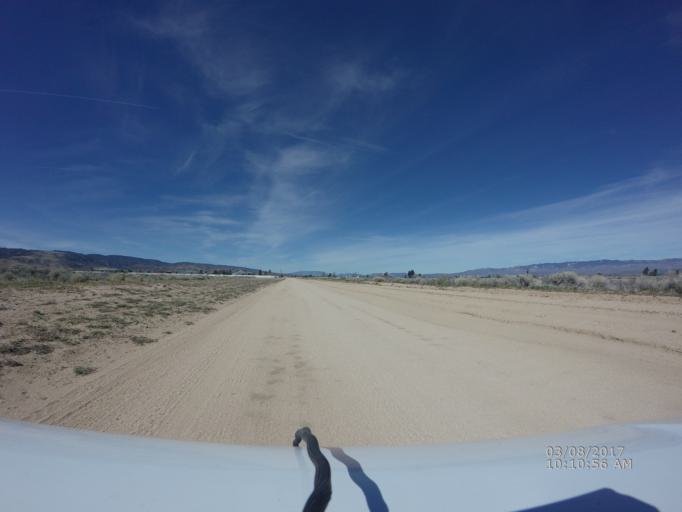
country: US
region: California
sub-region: Los Angeles County
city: Green Valley
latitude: 34.7532
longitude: -118.4447
